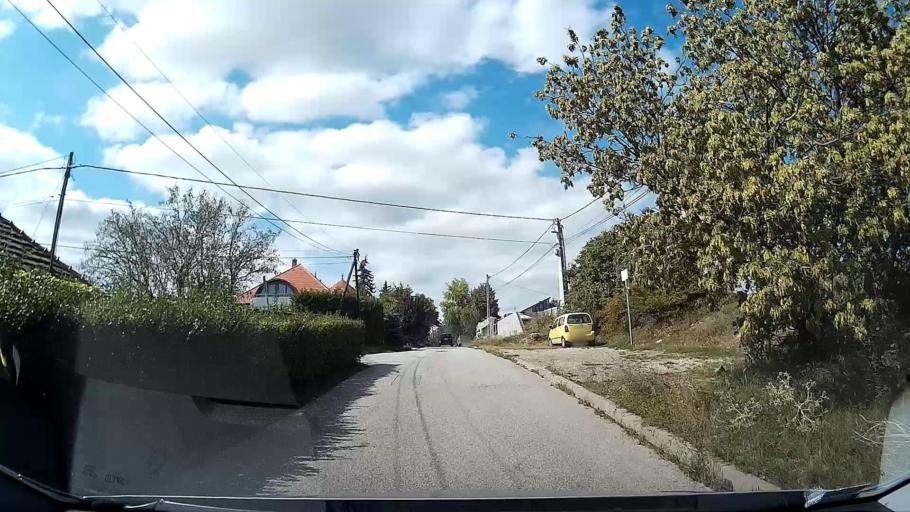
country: HU
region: Pest
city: Szentendre
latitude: 47.6897
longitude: 19.0723
